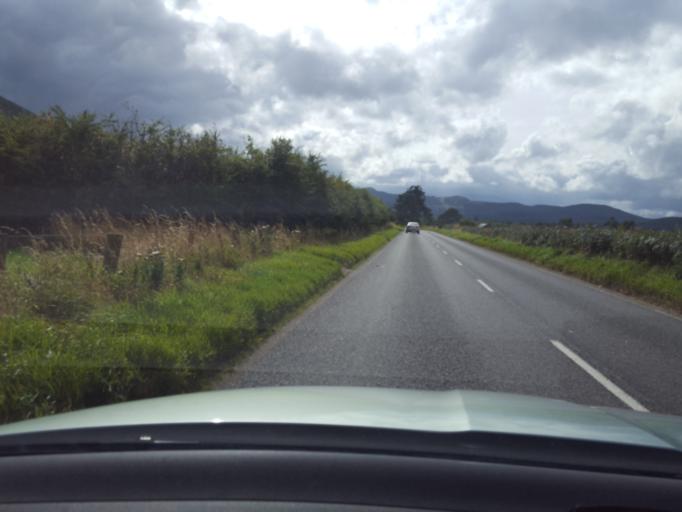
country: GB
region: Scotland
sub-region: Aberdeenshire
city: Ballater
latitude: 57.0574
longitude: -3.0242
